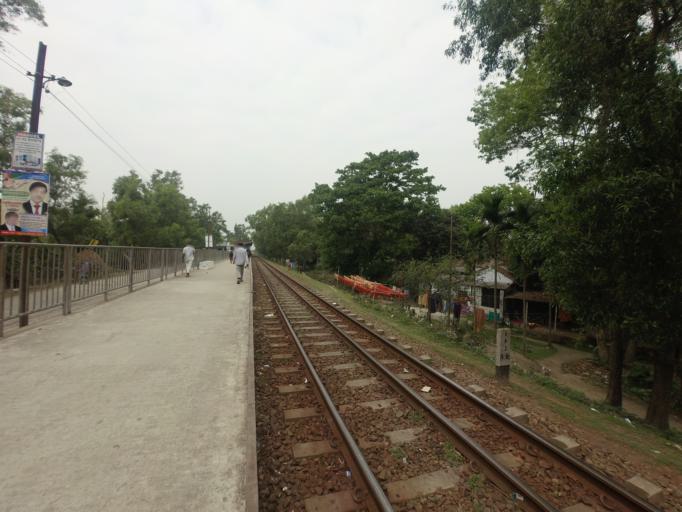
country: BD
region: Rajshahi
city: Sirajganj
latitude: 24.3971
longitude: 89.6912
